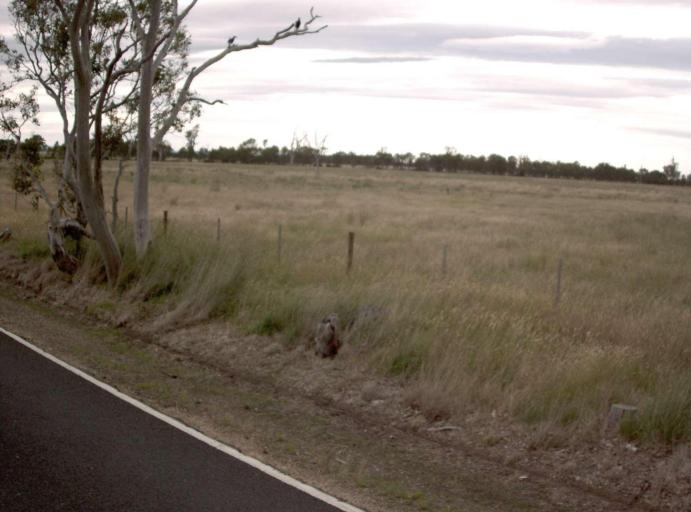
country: AU
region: Victoria
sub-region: Wellington
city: Sale
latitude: -37.9940
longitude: 147.1926
